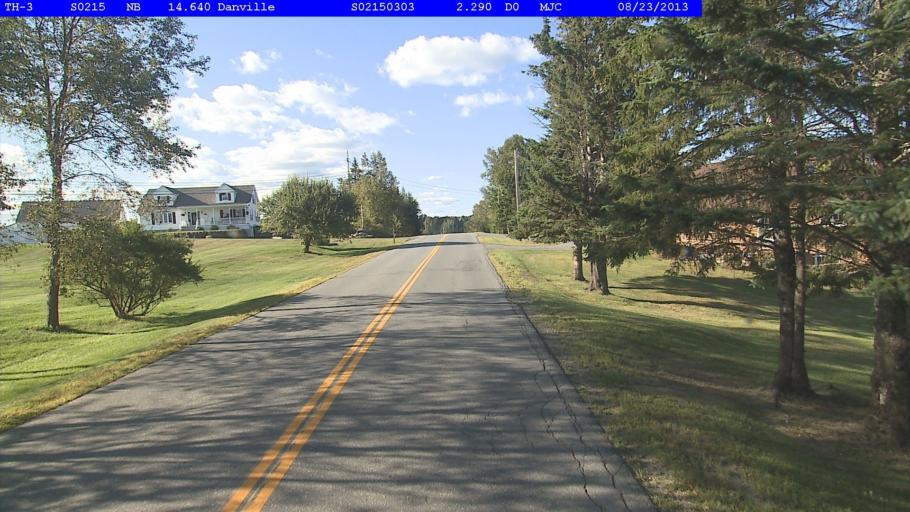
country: US
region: Vermont
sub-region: Caledonia County
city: Saint Johnsbury
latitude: 44.3978
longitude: -72.1400
